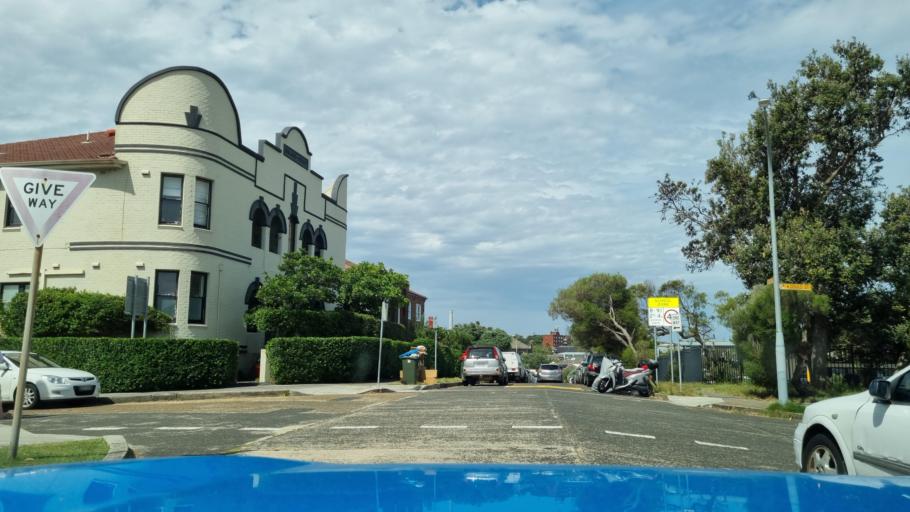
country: AU
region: New South Wales
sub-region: Waverley
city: North Bondi
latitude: -33.8862
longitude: 151.2775
